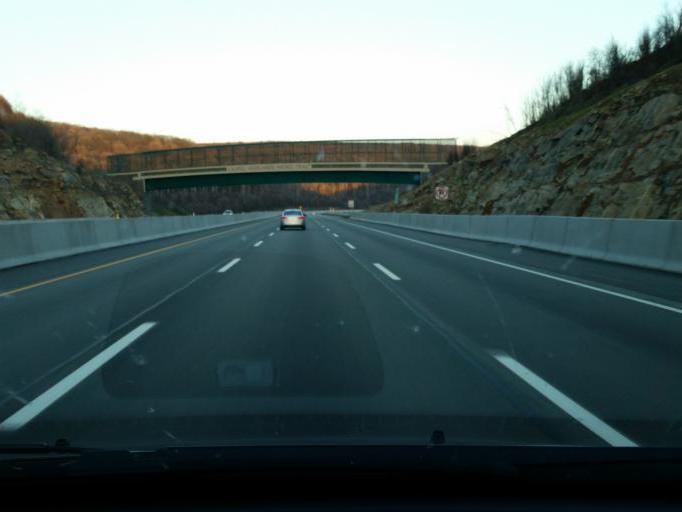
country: US
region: Pennsylvania
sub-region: Westmoreland County
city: Ligonier
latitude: 40.1049
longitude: -79.2104
